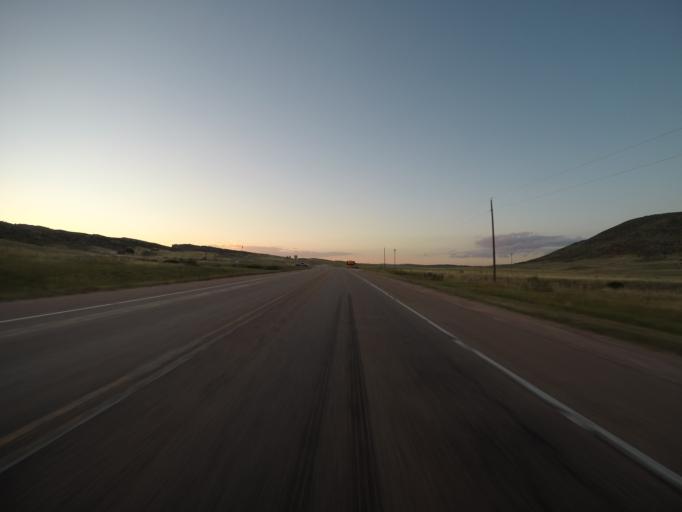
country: US
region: Colorado
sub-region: Larimer County
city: Laporte
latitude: 40.7511
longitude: -105.1706
